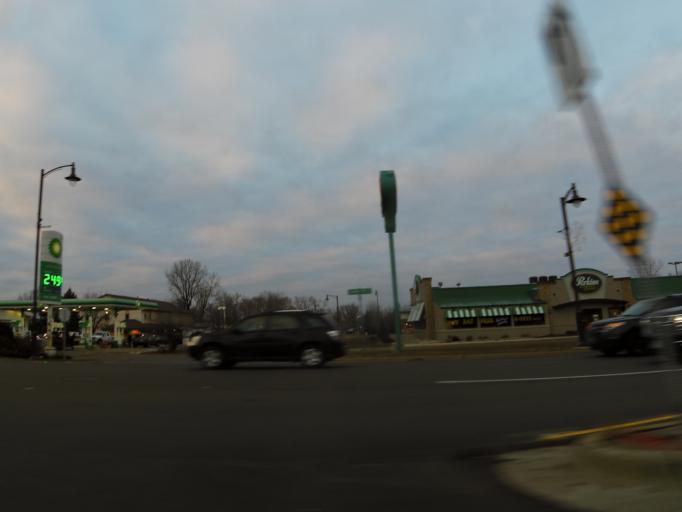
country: US
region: Minnesota
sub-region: Ramsey County
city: Vadnais Heights
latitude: 45.0502
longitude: -93.0563
